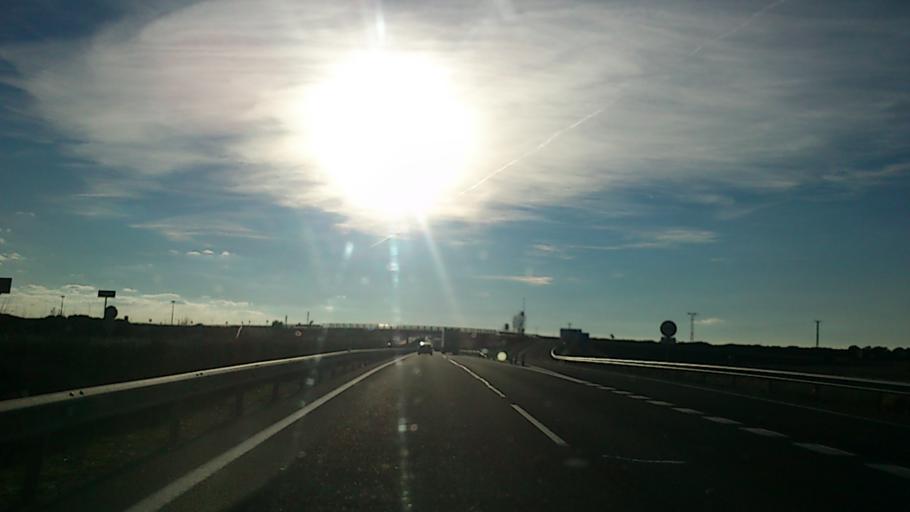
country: ES
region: Castille-La Mancha
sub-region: Provincia de Guadalajara
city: Mirabueno
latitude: 40.9321
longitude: -2.7115
